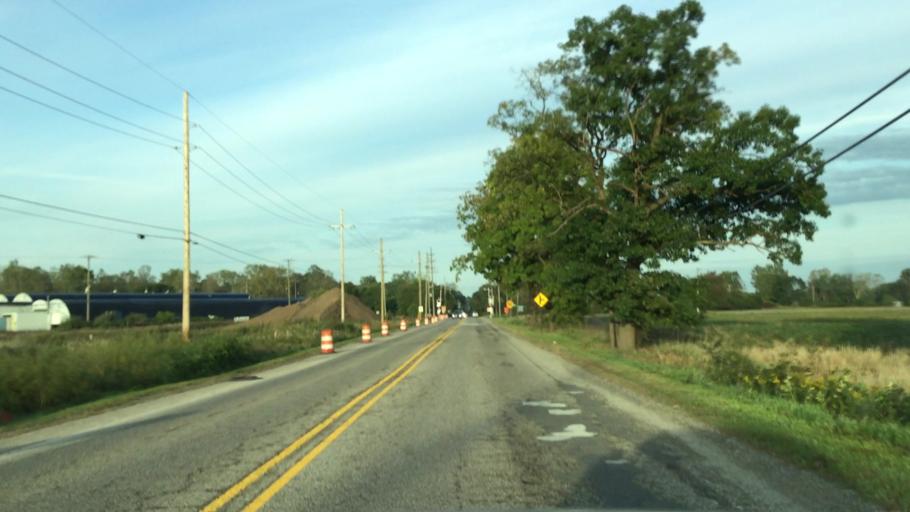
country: US
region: Michigan
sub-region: Livingston County
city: Whitmore Lake
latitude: 42.4291
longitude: -83.7722
